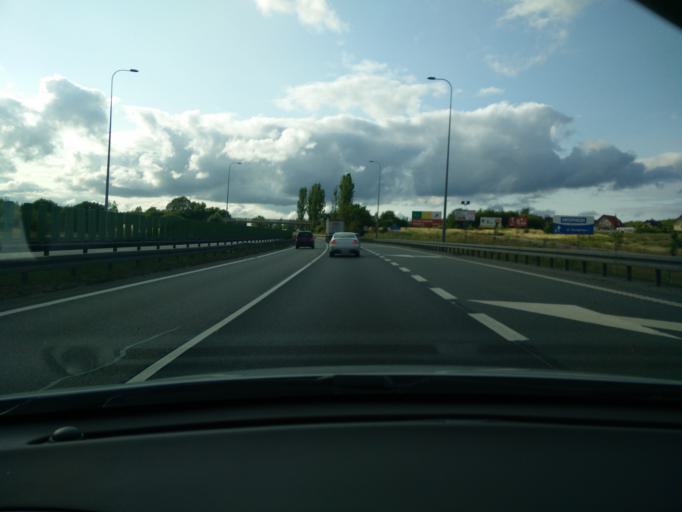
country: PL
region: Pomeranian Voivodeship
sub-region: Powiat gdanski
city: Straszyn
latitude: 54.2957
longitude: 18.5836
